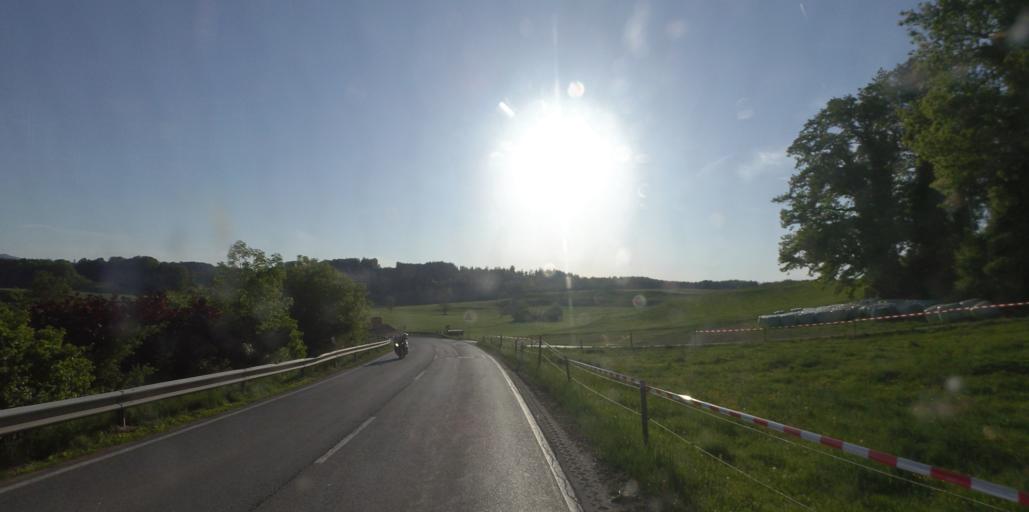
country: DE
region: Bavaria
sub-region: Upper Bavaria
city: Vachendorf
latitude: 47.8409
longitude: 12.6054
